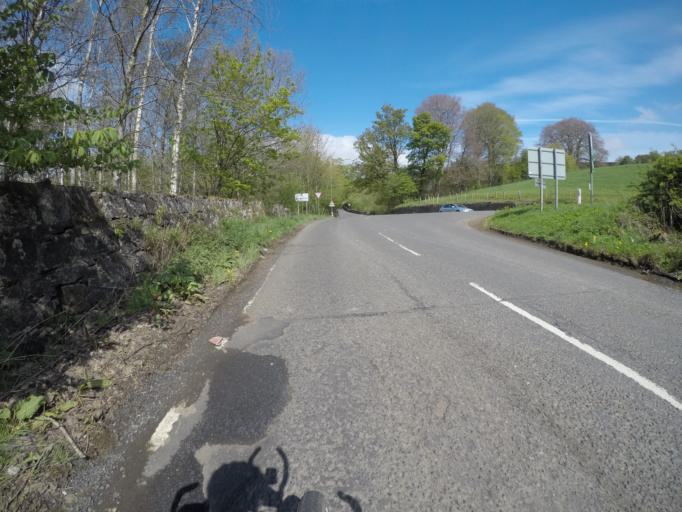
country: GB
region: Scotland
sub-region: East Ayrshire
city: Stewarton
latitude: 55.6764
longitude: -4.5213
